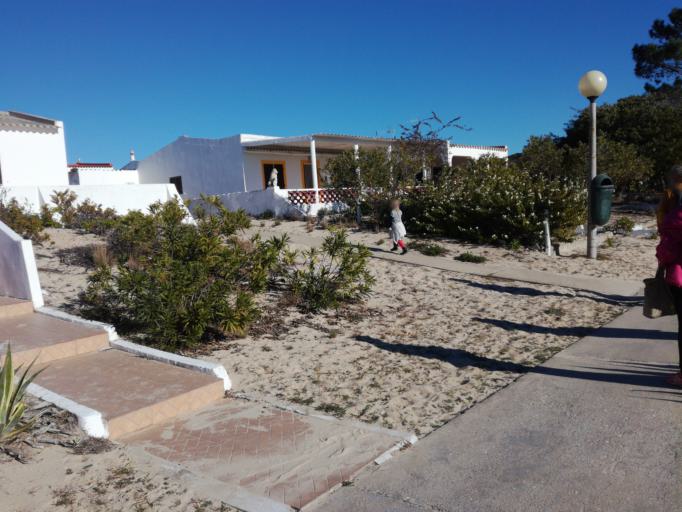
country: PT
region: Faro
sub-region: Olhao
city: Olhao
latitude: 37.0170
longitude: -7.7982
